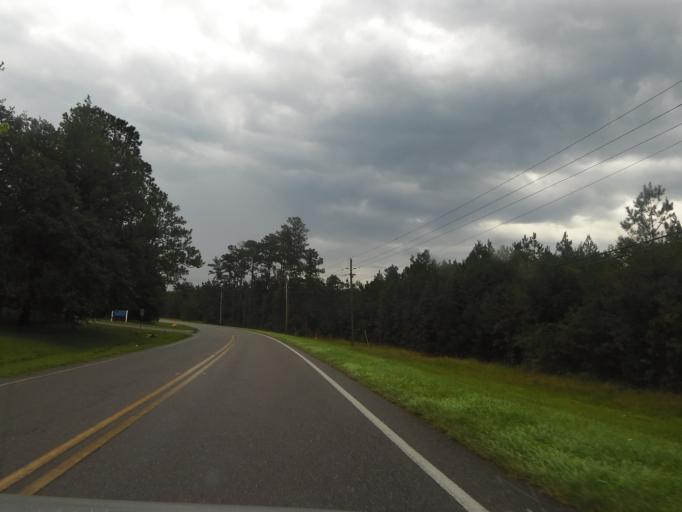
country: US
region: Florida
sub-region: Clay County
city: Middleburg
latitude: 30.0878
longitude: -81.8440
